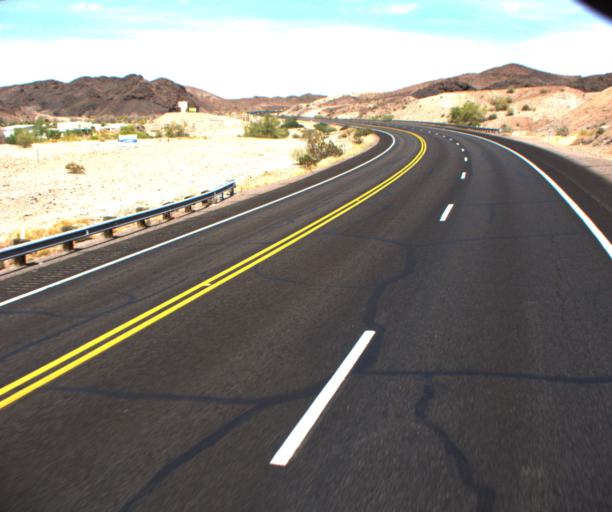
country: US
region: Arizona
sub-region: La Paz County
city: Cienega Springs
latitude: 34.1849
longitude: -114.2180
